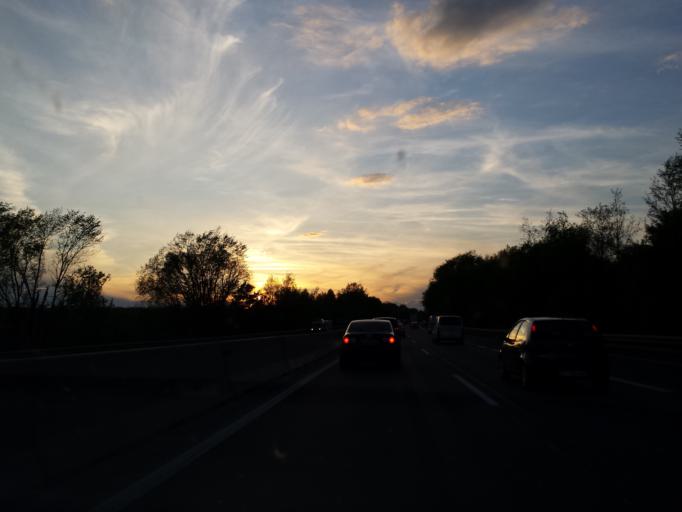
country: AT
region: Lower Austria
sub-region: Politischer Bezirk Bruck an der Leitha
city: Bruck an der Leitha
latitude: 48.0593
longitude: 16.7074
